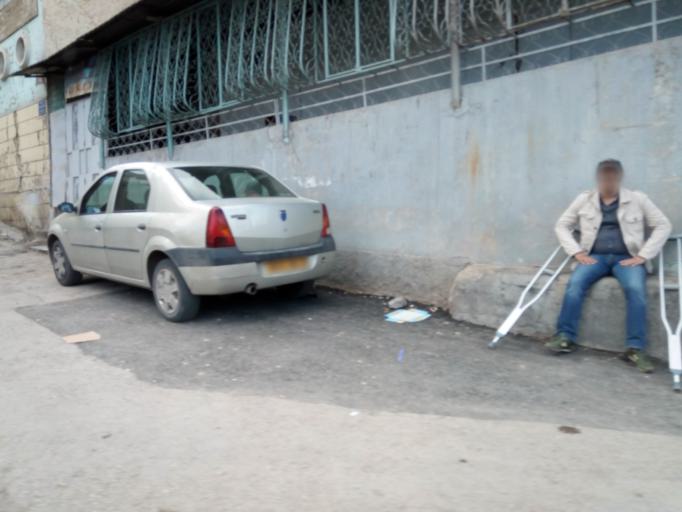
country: DZ
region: Constantine
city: Constantine
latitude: 36.3643
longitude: 6.6112
